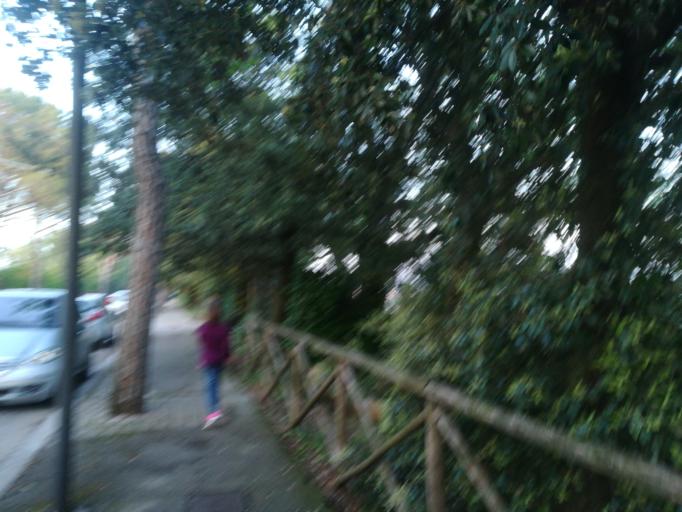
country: IT
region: The Marches
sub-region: Provincia di Macerata
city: Villa Potenza
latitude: 43.2920
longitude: 13.4173
